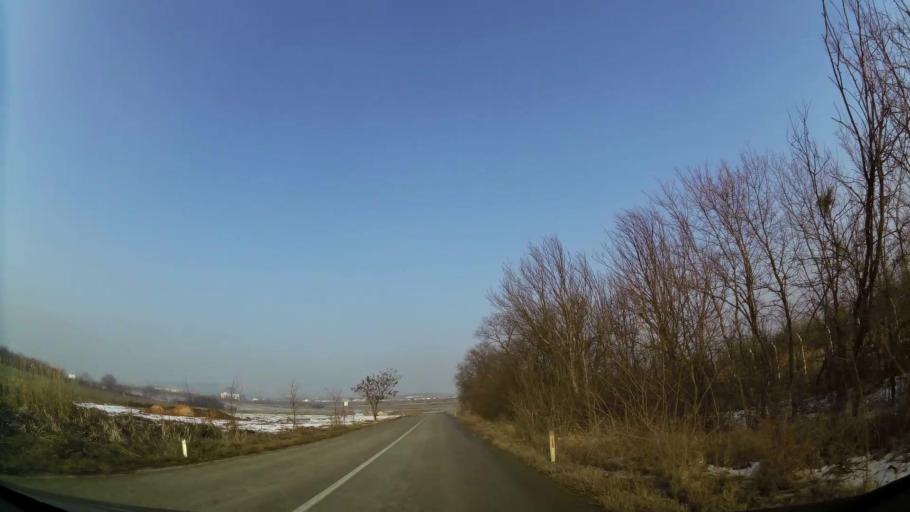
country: MK
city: Kadino
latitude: 41.9773
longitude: 21.6116
